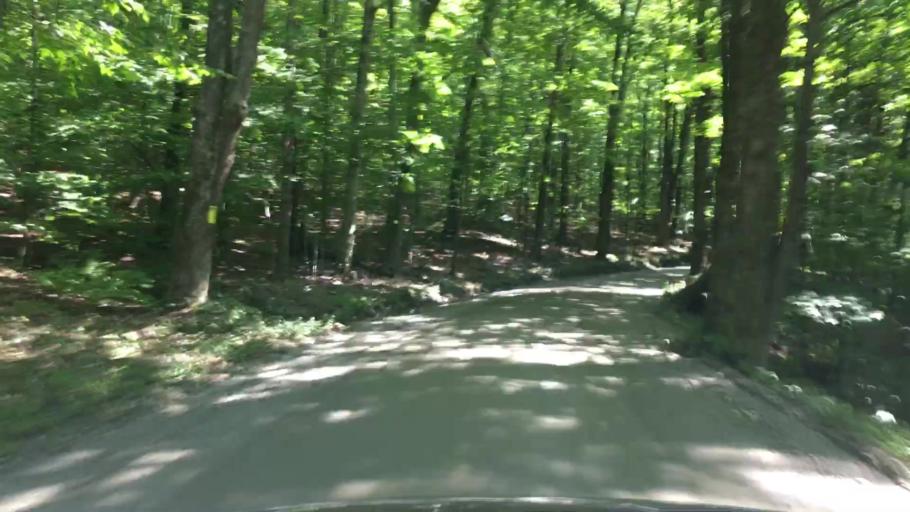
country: US
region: Vermont
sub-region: Windham County
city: West Brattleboro
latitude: 42.8024
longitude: -72.6462
